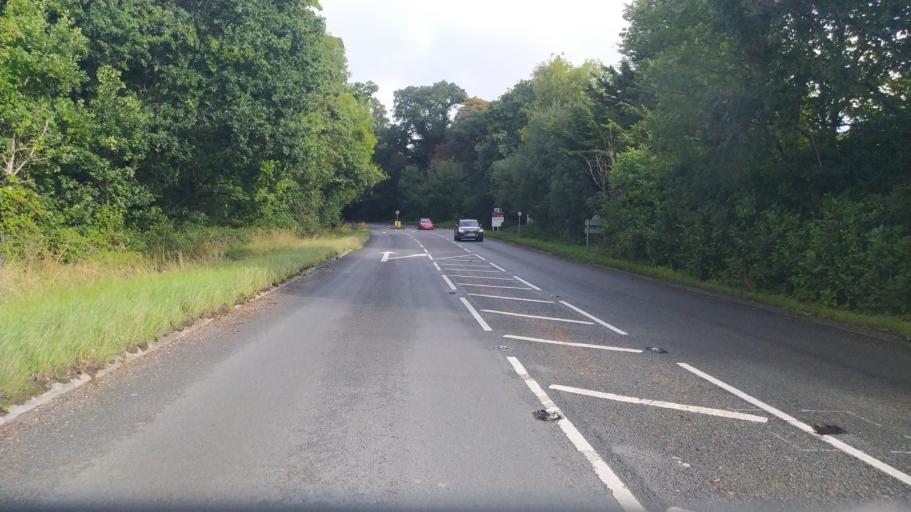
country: GB
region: England
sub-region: Hampshire
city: Totton
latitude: 50.9354
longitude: -1.5123
